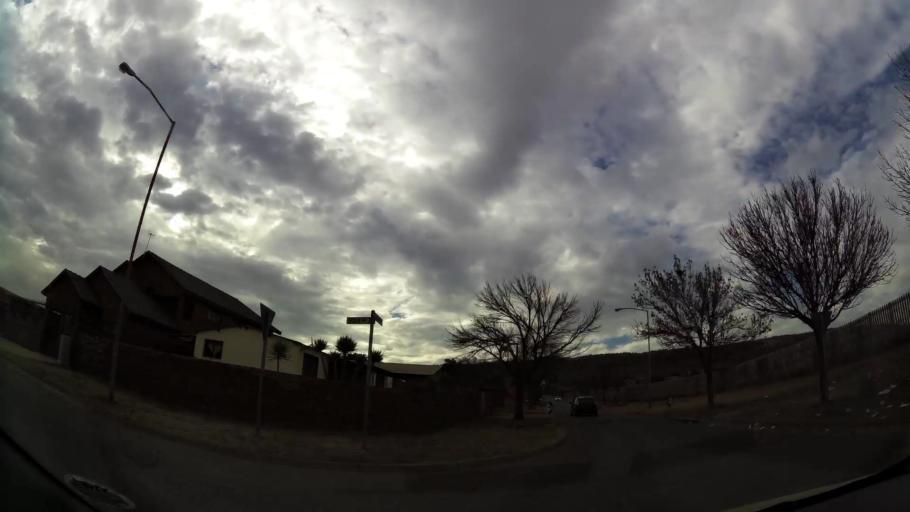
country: ZA
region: Gauteng
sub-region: City of Tshwane Metropolitan Municipality
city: Pretoria
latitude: -25.7021
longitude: 28.3127
